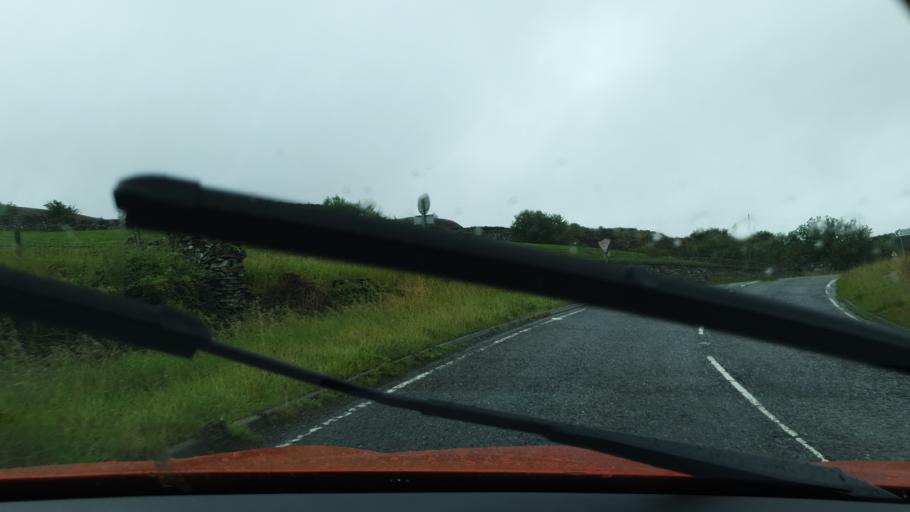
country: GB
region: England
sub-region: Cumbria
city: Ulverston
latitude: 54.2529
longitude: -3.1220
